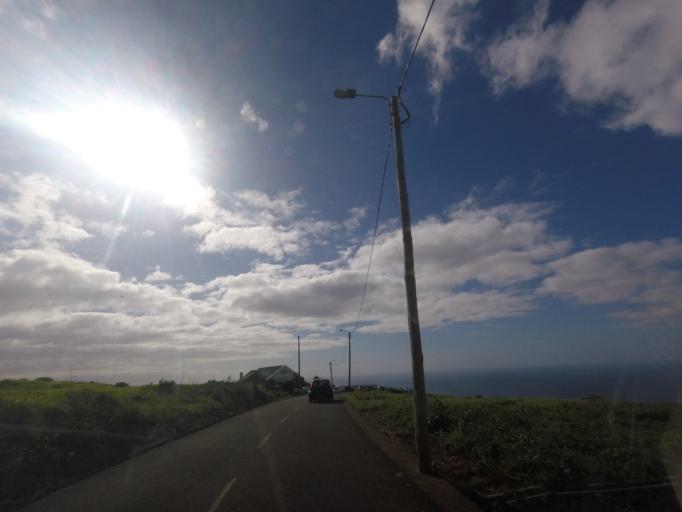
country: PT
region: Madeira
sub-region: Calheta
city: Faja da Ovelha
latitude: 32.8105
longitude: -17.2561
